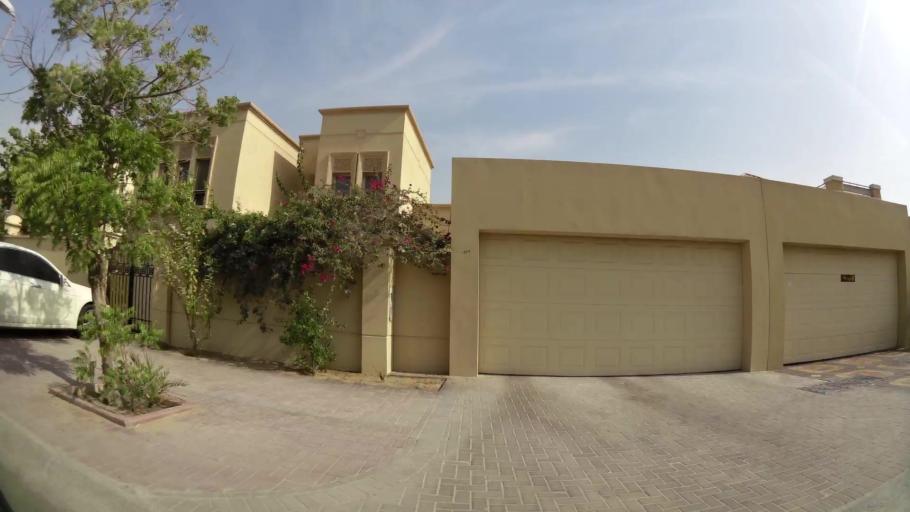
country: AE
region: Ash Shariqah
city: Sharjah
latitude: 25.2625
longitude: 55.4472
